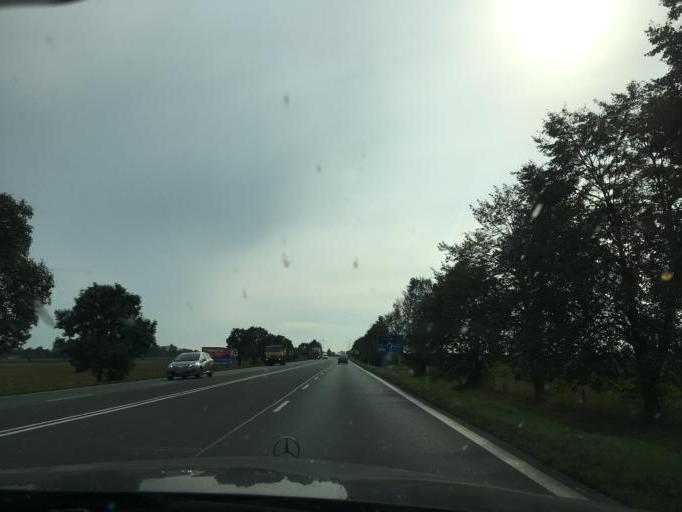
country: CZ
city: Stezery
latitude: 50.2139
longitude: 15.7849
